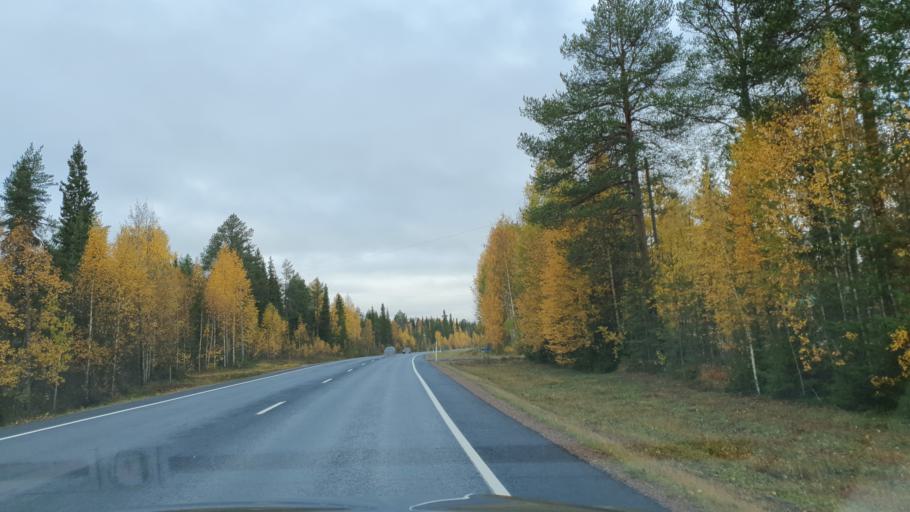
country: FI
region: Lapland
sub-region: Rovaniemi
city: Rovaniemi
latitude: 66.6146
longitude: 25.5520
